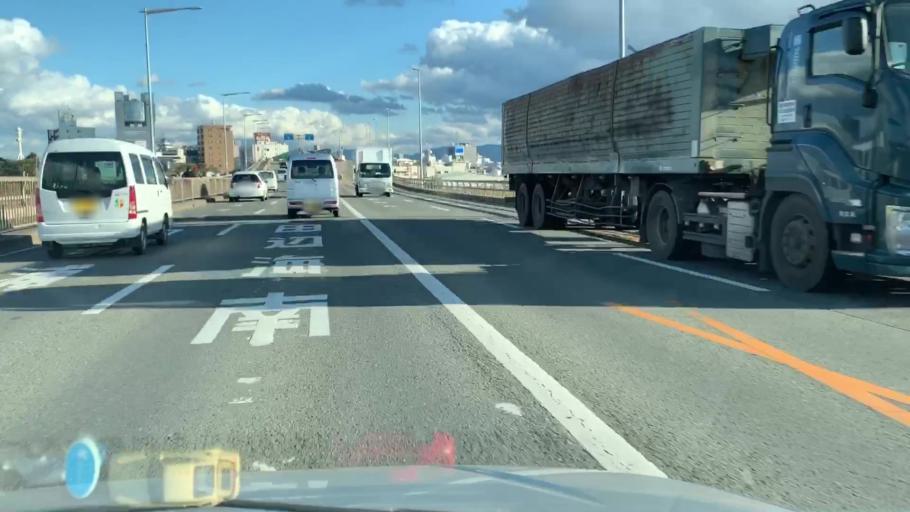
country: JP
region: Wakayama
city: Wakayama-shi
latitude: 34.2319
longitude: 135.1583
